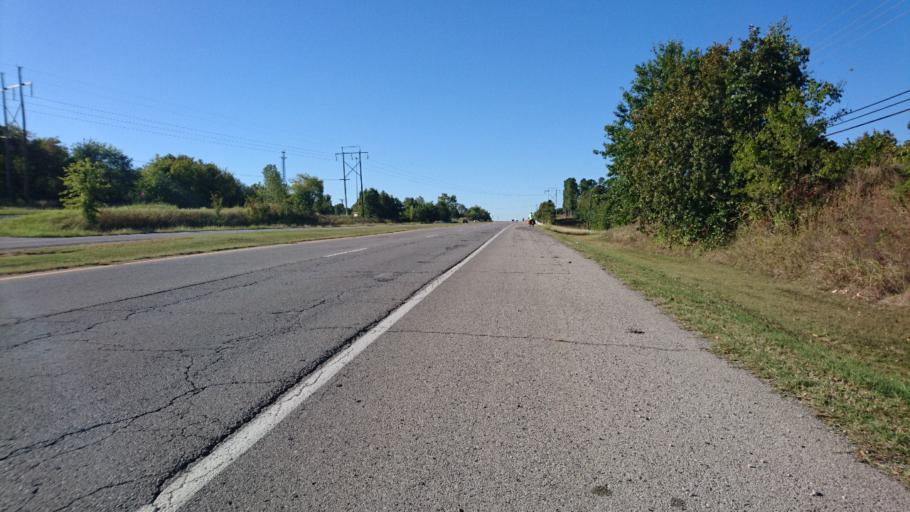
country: US
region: Oklahoma
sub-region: Rogers County
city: Catoosa
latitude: 36.2052
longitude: -95.7266
